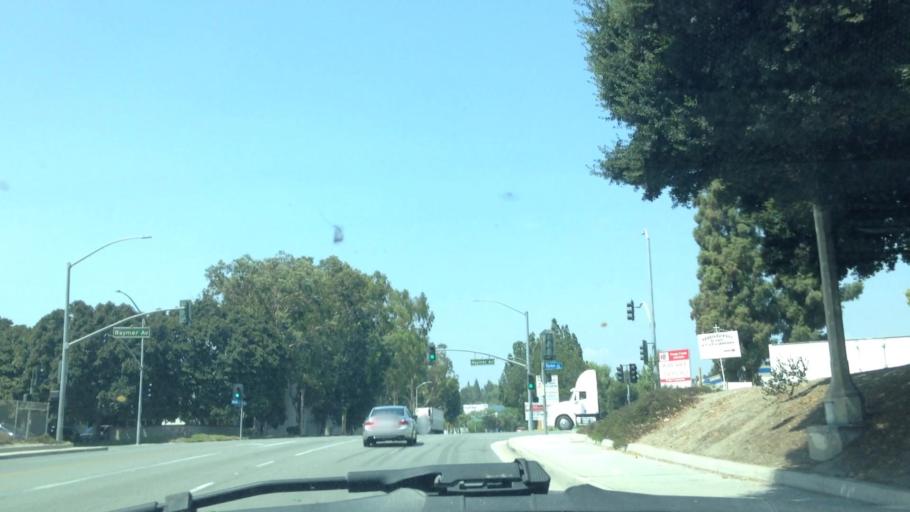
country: US
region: California
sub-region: Orange County
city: Buena Park
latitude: 33.8732
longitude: -117.9682
